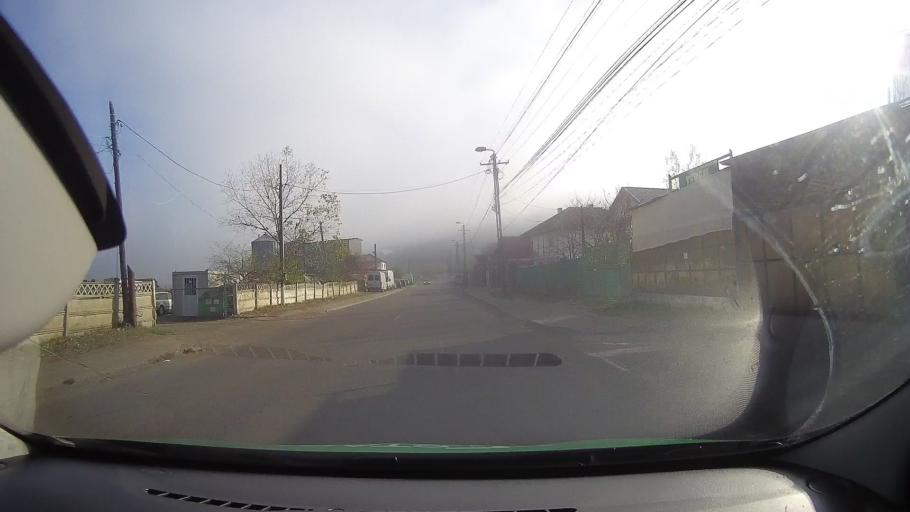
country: RO
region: Tulcea
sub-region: Municipiul Tulcea
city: Tulcea
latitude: 45.1655
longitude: 28.8231
